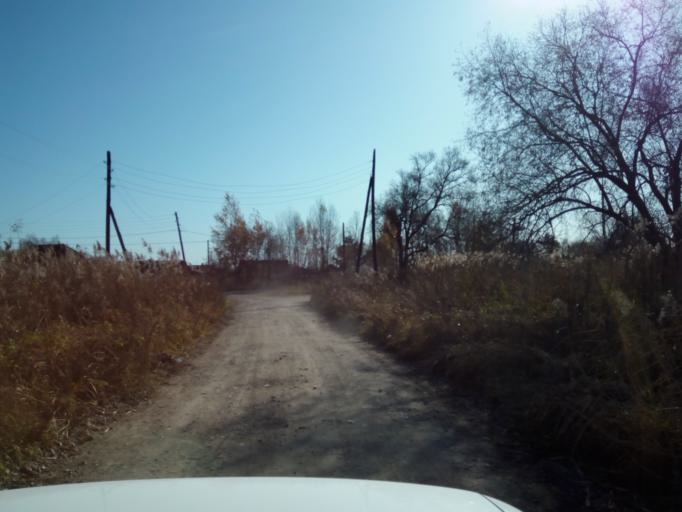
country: RU
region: Primorskiy
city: Dal'nerechensk
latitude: 45.9125
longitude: 133.8022
